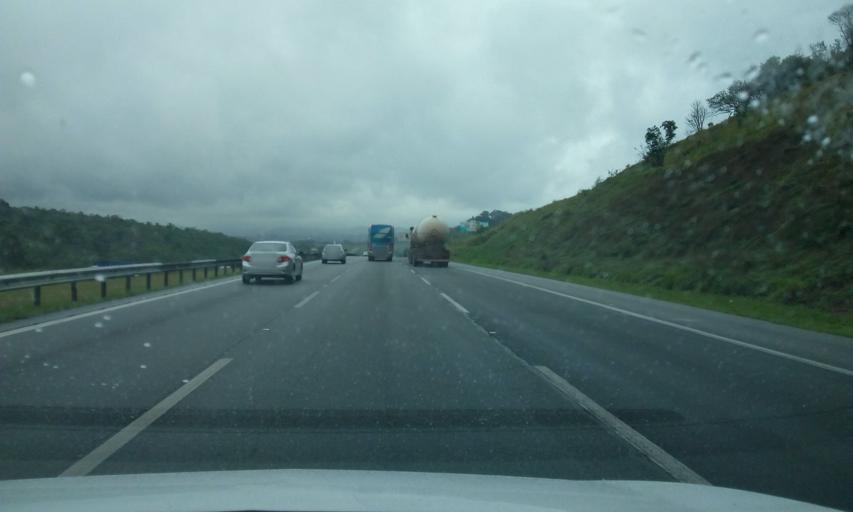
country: BR
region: Sao Paulo
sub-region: Jundiai
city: Jundiai
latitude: -23.2269
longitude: -46.9026
